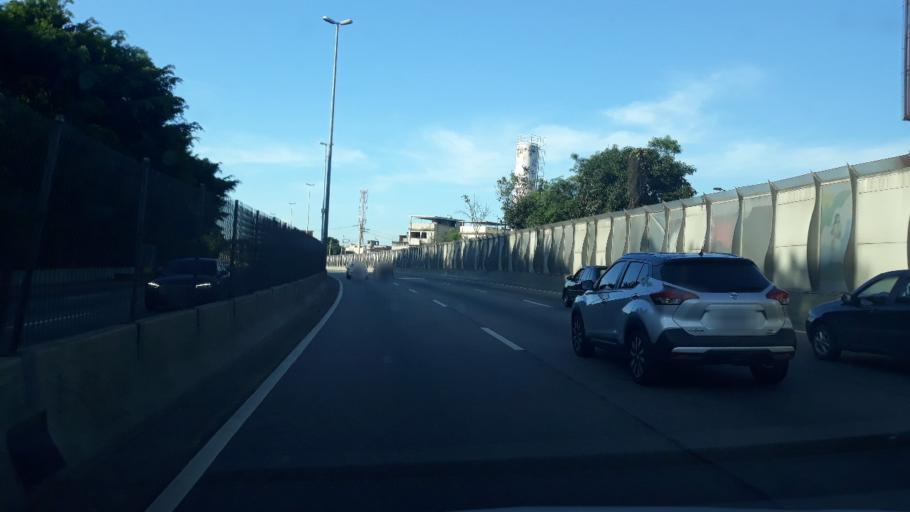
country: BR
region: Rio de Janeiro
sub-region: Sao Joao De Meriti
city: Sao Joao de Meriti
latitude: -22.9492
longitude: -43.3562
